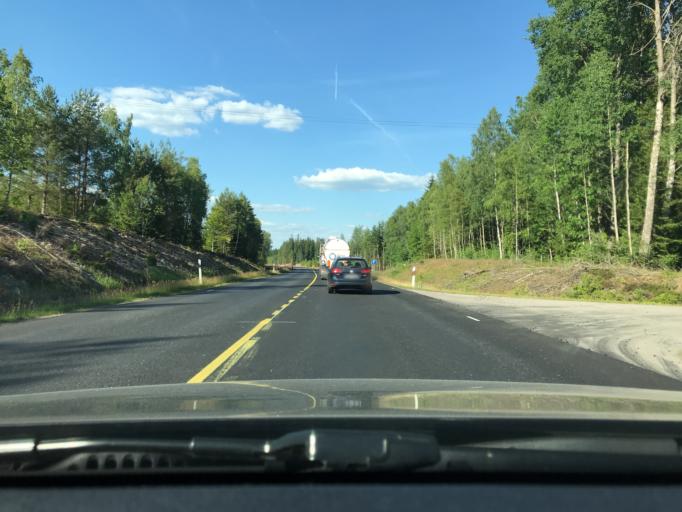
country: SE
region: Kronoberg
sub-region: Almhults Kommun
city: AElmhult
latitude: 56.6263
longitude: 14.2518
